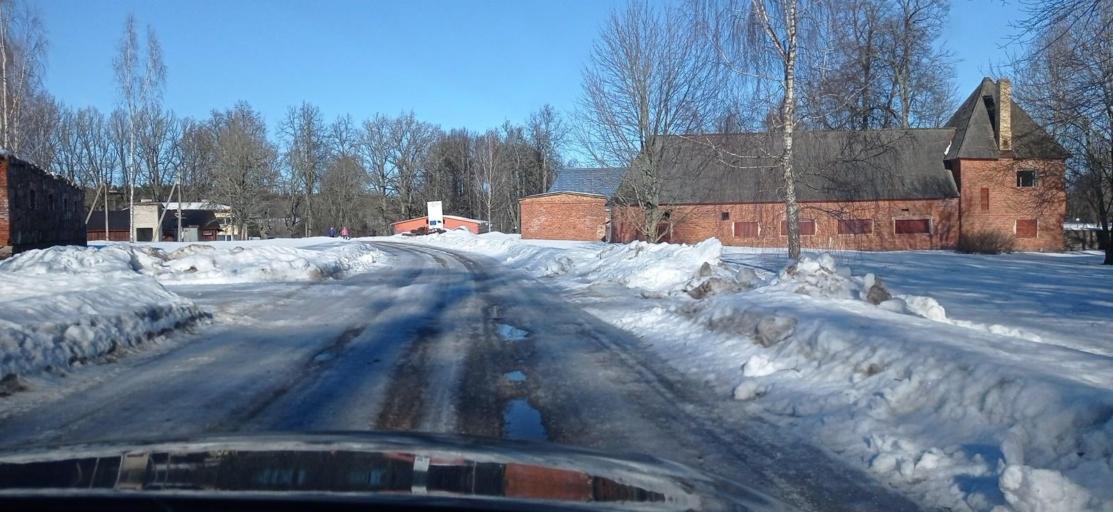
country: EE
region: Tartu
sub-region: Alatskivi vald
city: Kallaste
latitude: 58.6023
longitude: 27.1277
